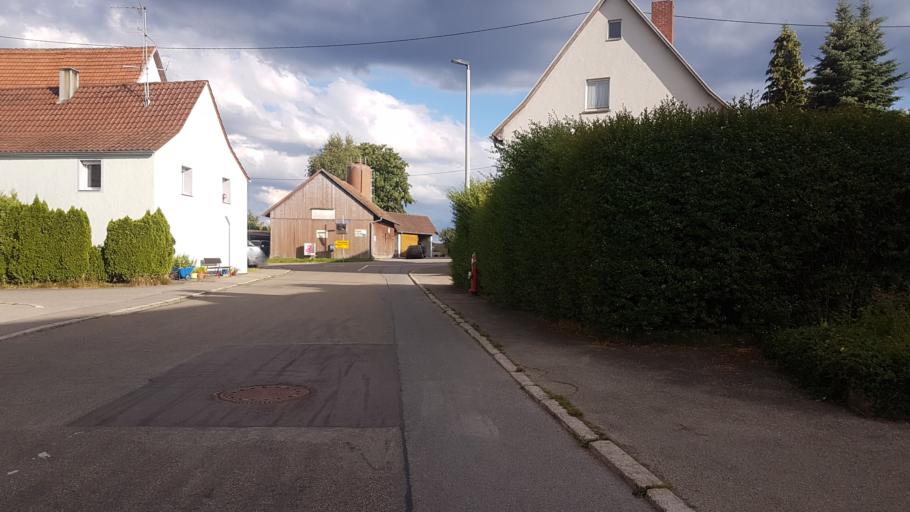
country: DE
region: Baden-Wuerttemberg
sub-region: Freiburg Region
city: Braunlingen
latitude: 47.9991
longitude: 8.4105
